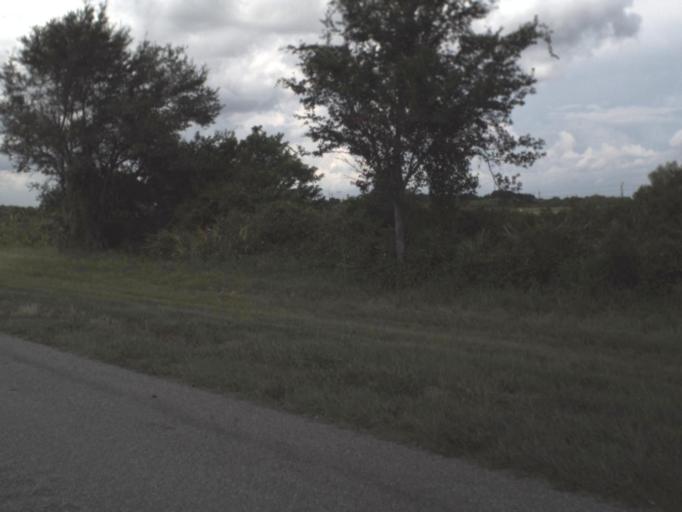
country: US
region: Florida
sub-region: Hillsborough County
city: Apollo Beach
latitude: 27.7555
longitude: -82.3745
